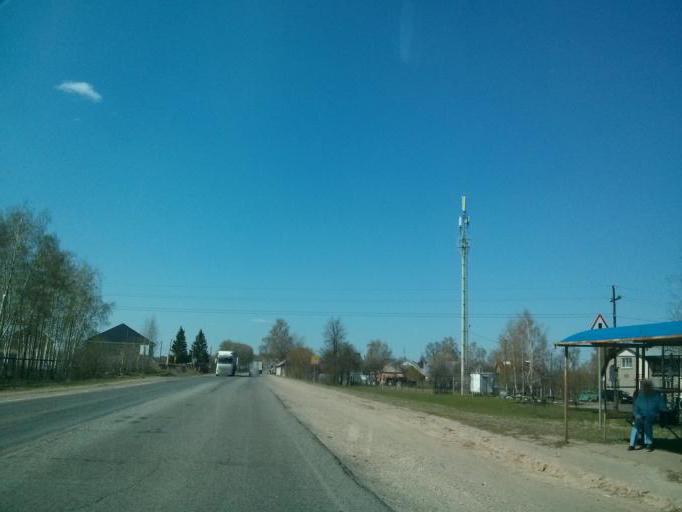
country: RU
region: Nizjnij Novgorod
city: Nizhniy Novgorod
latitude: 56.2117
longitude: 43.9717
